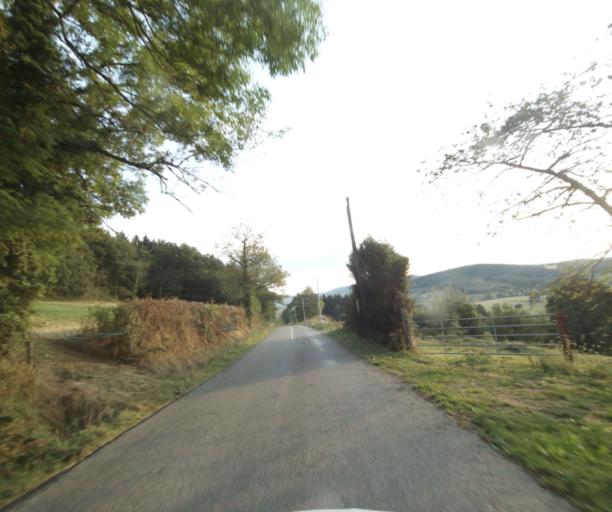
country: FR
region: Bourgogne
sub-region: Departement de Saone-et-Loire
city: Charolles
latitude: 46.3998
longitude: 4.3982
